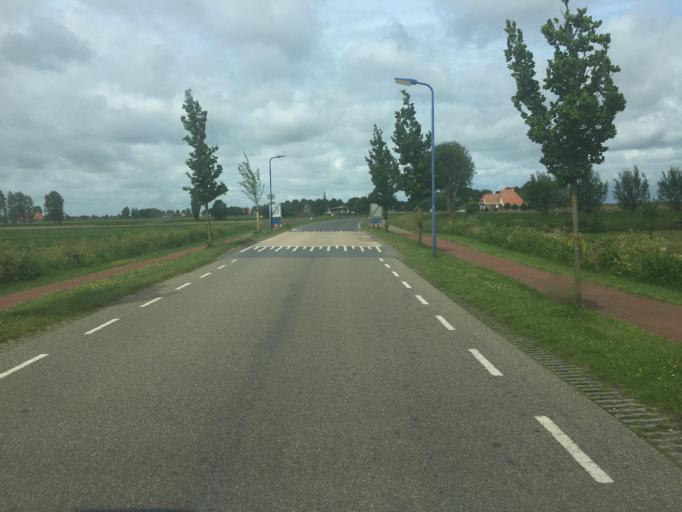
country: NL
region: Friesland
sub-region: Gemeente Lemsterland
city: Echtenerbrug
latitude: 52.8723
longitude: 5.8133
